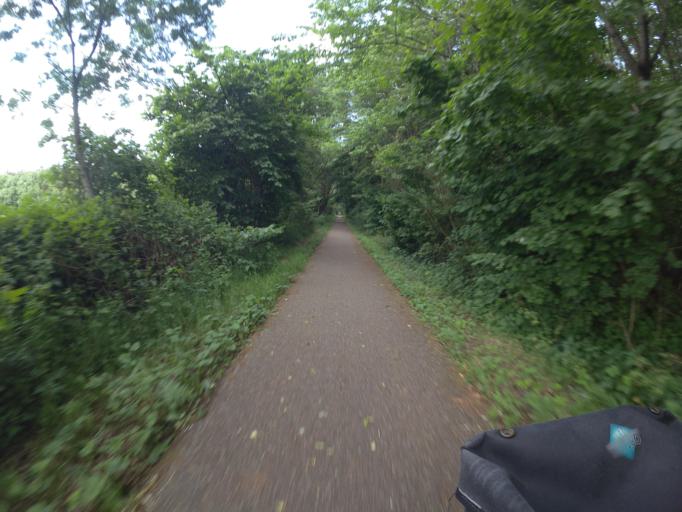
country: NL
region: Drenthe
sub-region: Gemeente Westerveld
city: Dwingeloo
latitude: 52.9068
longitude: 6.4528
